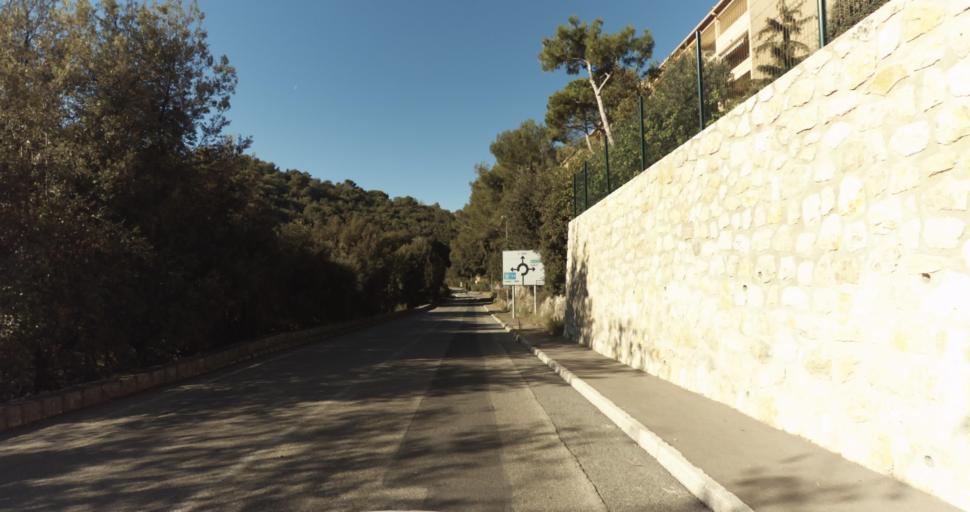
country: FR
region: Provence-Alpes-Cote d'Azur
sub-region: Departement des Alpes-Maritimes
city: Vence
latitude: 43.7151
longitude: 7.1183
